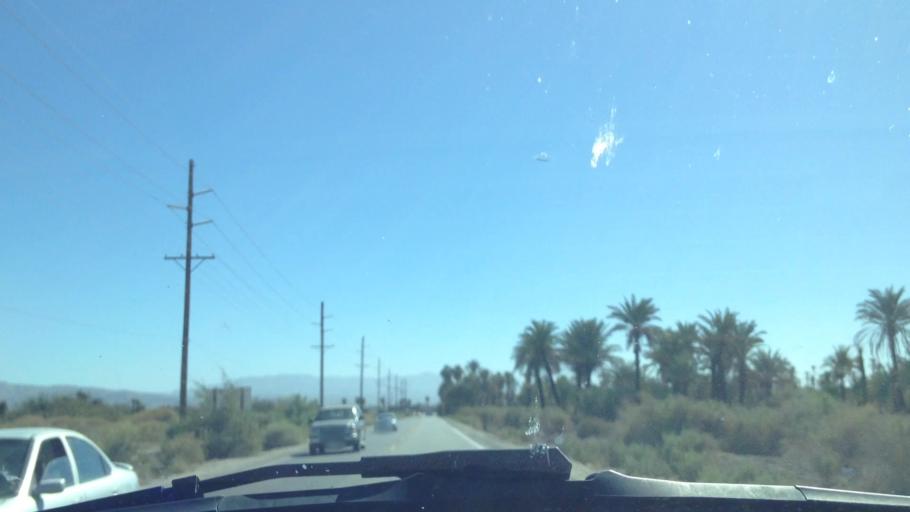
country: US
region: California
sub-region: Riverside County
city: Mecca
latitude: 33.5693
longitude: -116.0860
